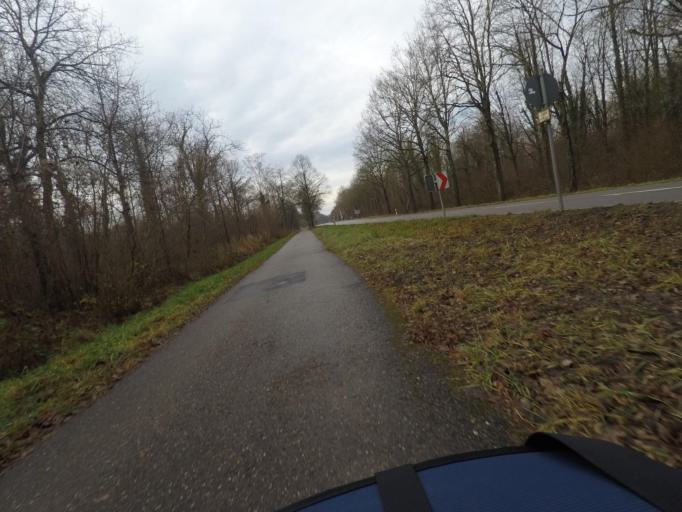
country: DE
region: Baden-Wuerttemberg
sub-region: Karlsruhe Region
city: Rheinau
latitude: 48.8533
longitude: 8.1817
